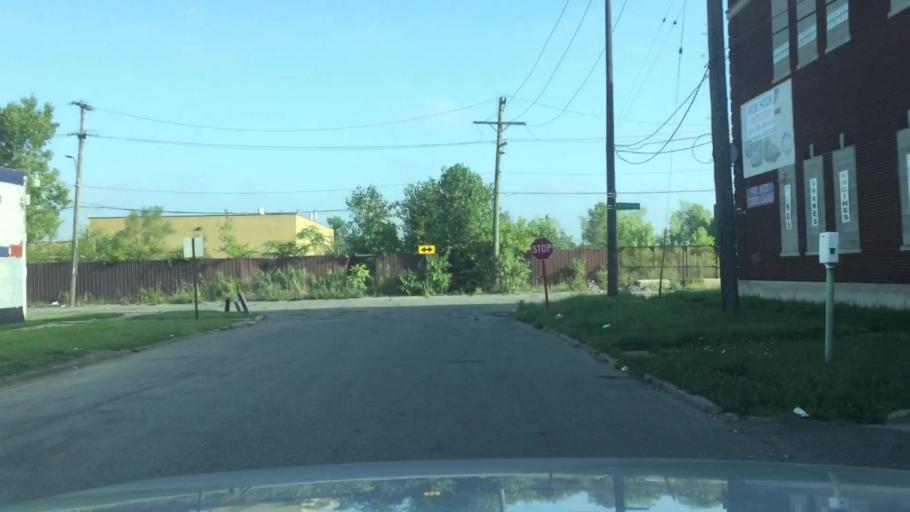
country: US
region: Michigan
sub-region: Wayne County
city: Dearborn
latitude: 42.3660
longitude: -83.1499
